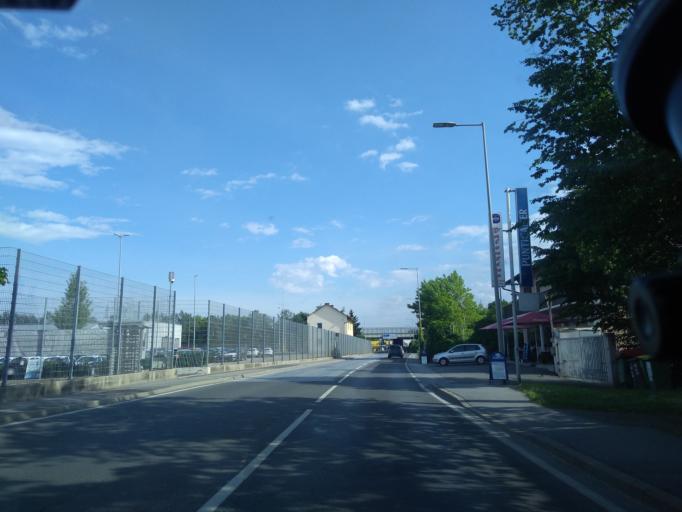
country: AT
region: Styria
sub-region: Politischer Bezirk Graz-Umgebung
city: Feldkirchen bei Graz
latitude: 47.0180
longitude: 15.4726
